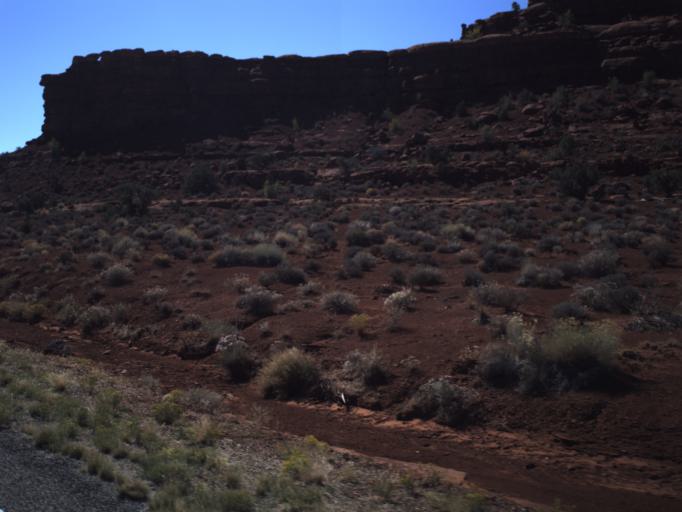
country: US
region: Utah
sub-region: San Juan County
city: Blanding
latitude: 37.7852
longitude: -110.2948
